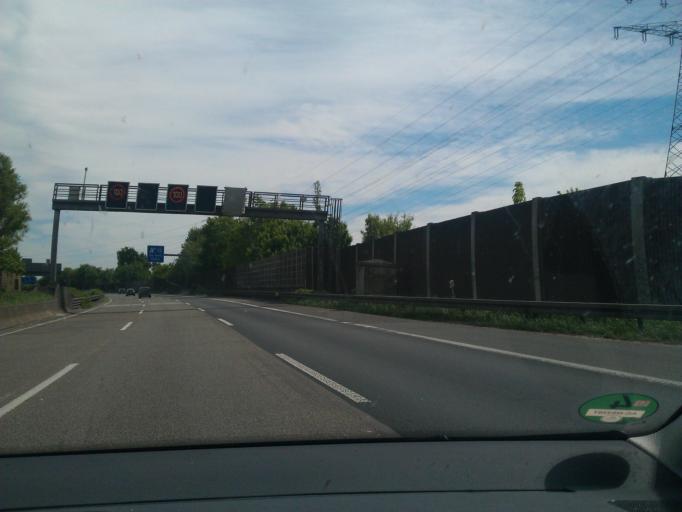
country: DE
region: North Rhine-Westphalia
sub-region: Regierungsbezirk Dusseldorf
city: Neuss
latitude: 51.1749
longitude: 6.7141
